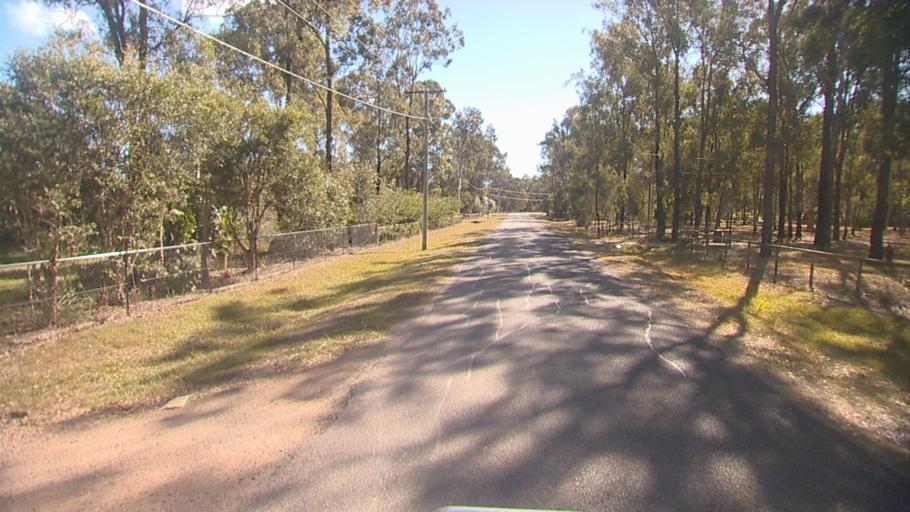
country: AU
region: Queensland
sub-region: Logan
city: Chambers Flat
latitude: -27.7459
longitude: 153.0948
